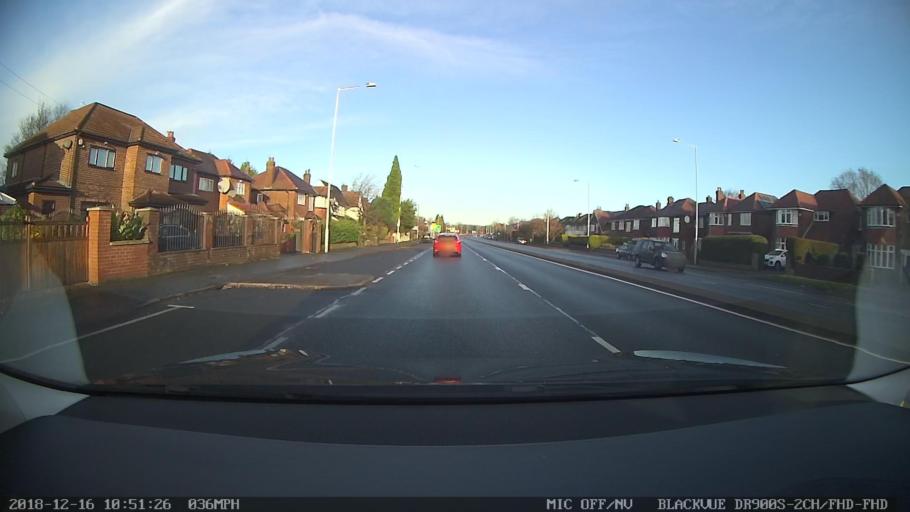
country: GB
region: England
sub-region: Manchester
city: Didsbury
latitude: 53.3880
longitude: -2.2250
